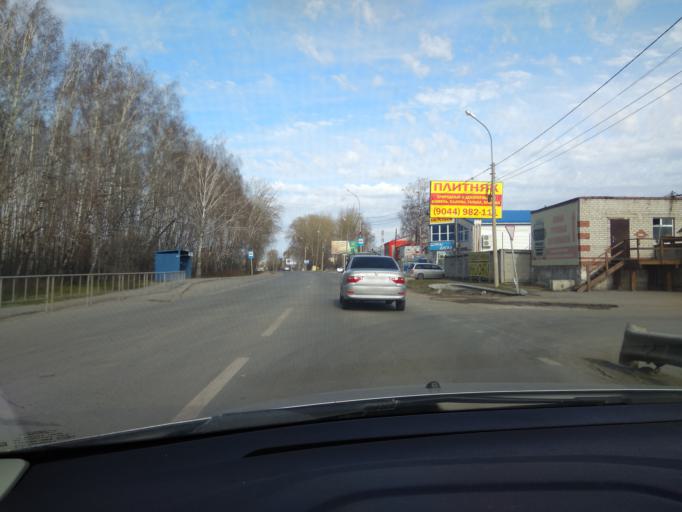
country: RU
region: Tjumen
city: Moskovskiy
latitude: 57.1552
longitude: 65.4415
